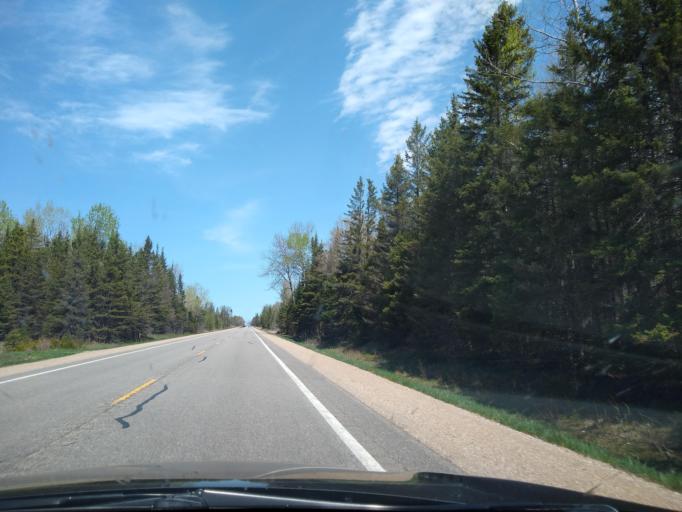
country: US
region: Michigan
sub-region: Delta County
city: Gladstone
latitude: 46.0530
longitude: -86.9813
